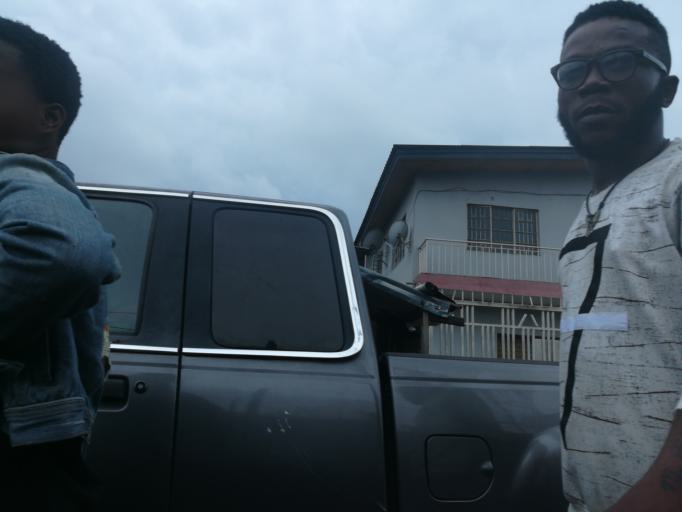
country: NG
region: Lagos
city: Ojota
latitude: 6.5726
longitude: 3.3719
